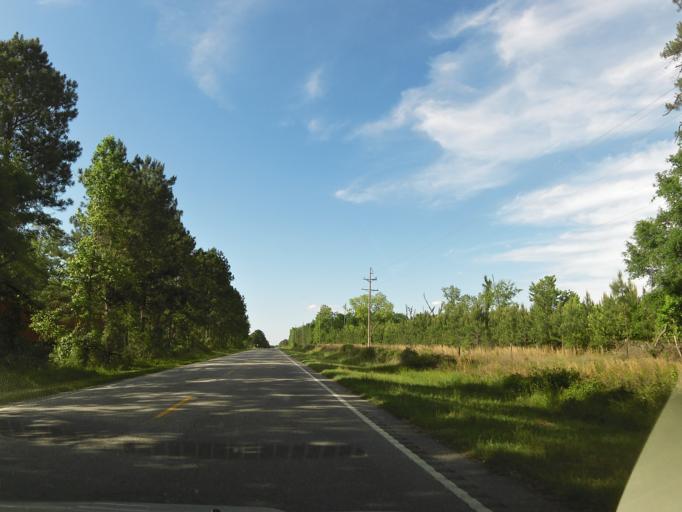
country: US
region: South Carolina
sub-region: Allendale County
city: Fairfax
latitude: 32.9179
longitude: -81.2375
